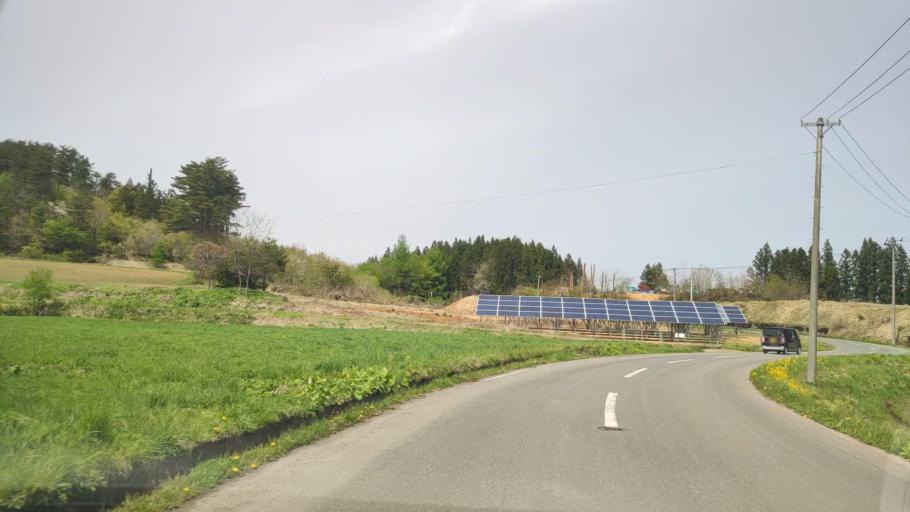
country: JP
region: Aomori
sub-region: Misawa Shi
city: Inuotose
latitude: 40.7714
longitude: 141.1226
